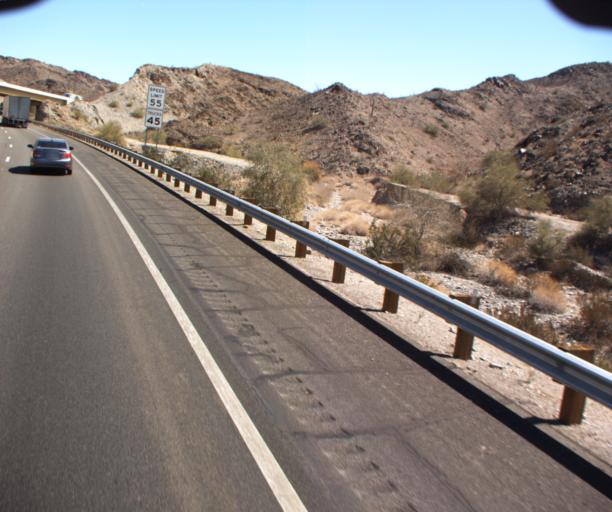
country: US
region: Arizona
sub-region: Yuma County
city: Fortuna Foothills
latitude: 32.6590
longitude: -114.3352
